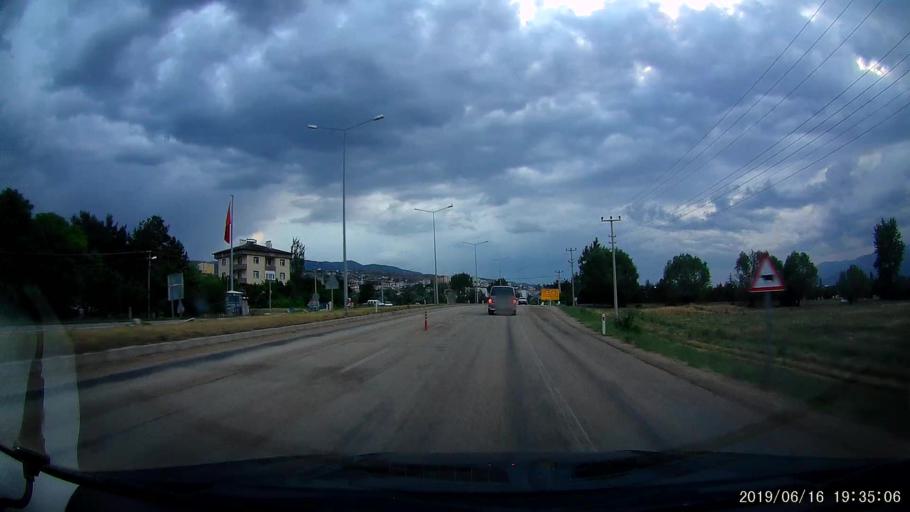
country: TR
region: Sivas
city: Susehri
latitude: 40.1688
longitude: 38.0977
